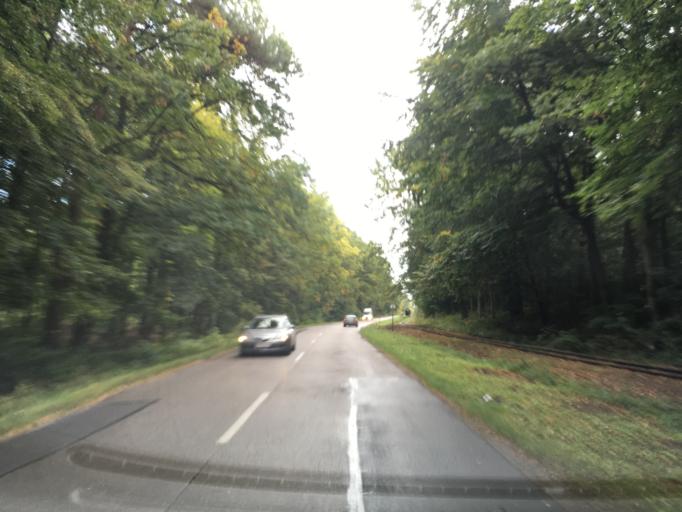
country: PL
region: Pomeranian Voivodeship
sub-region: Powiat nowodworski
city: Stegna
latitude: 54.3319
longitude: 19.0865
